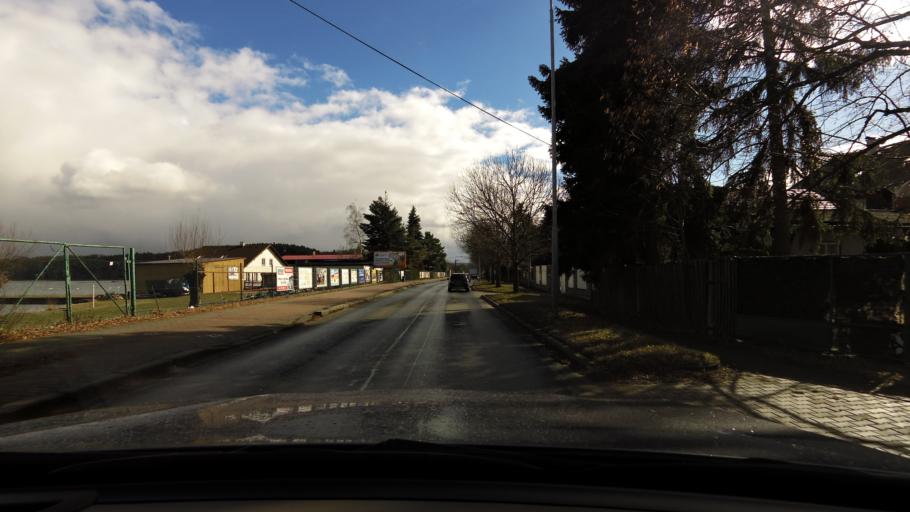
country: CZ
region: Plzensky
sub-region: Okres Plzen-Mesto
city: Pilsen
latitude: 49.7725
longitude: 13.3945
